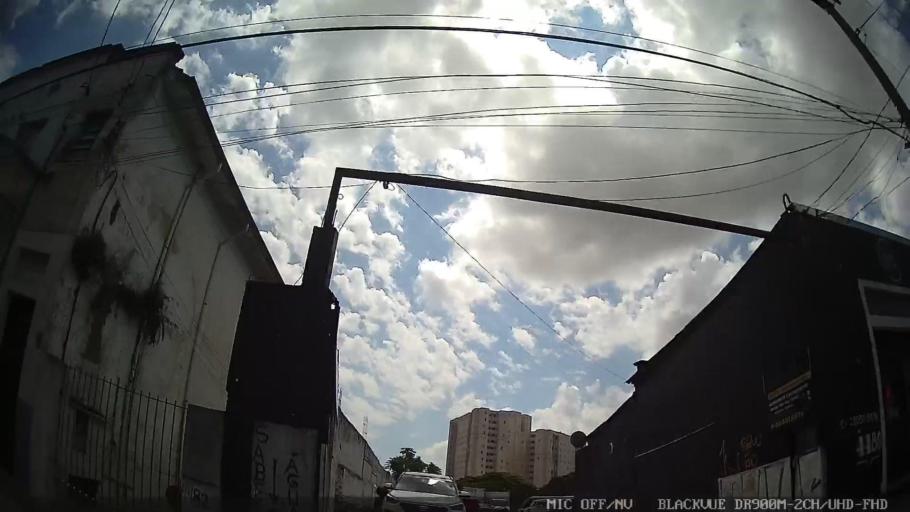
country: BR
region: Sao Paulo
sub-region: Ferraz De Vasconcelos
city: Ferraz de Vasconcelos
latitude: -23.5320
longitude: -46.4534
